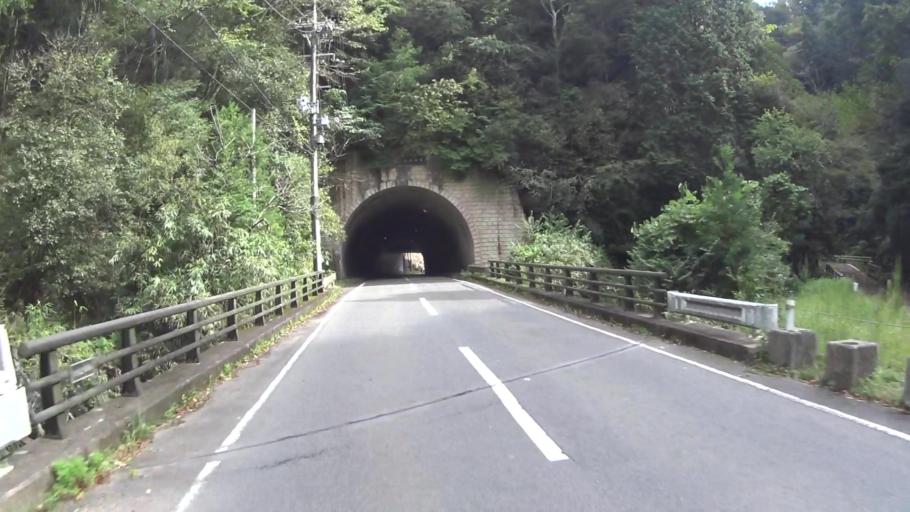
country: JP
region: Kyoto
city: Uji
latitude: 34.9210
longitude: 135.8566
